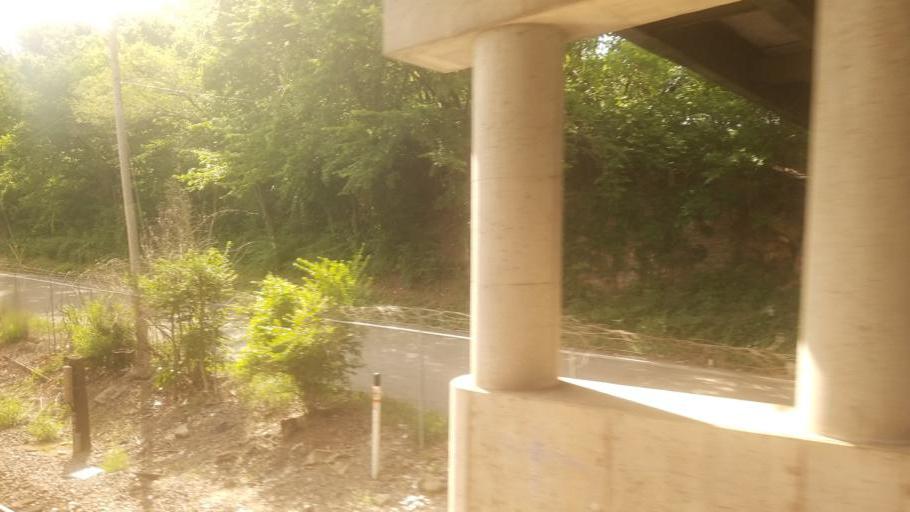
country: US
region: Kansas
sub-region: Johnson County
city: Westwood
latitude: 39.0742
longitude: -94.6241
